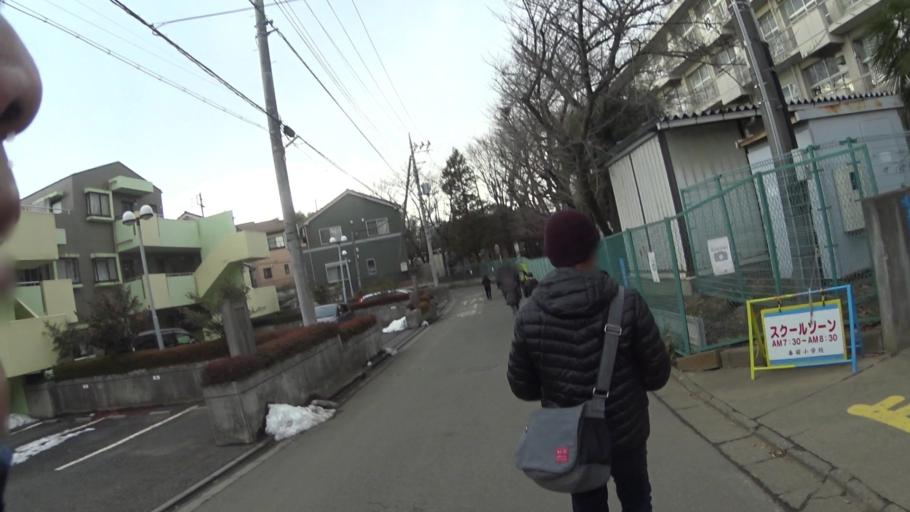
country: JP
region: Saitama
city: Shimotoda
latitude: 35.8527
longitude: 139.6863
